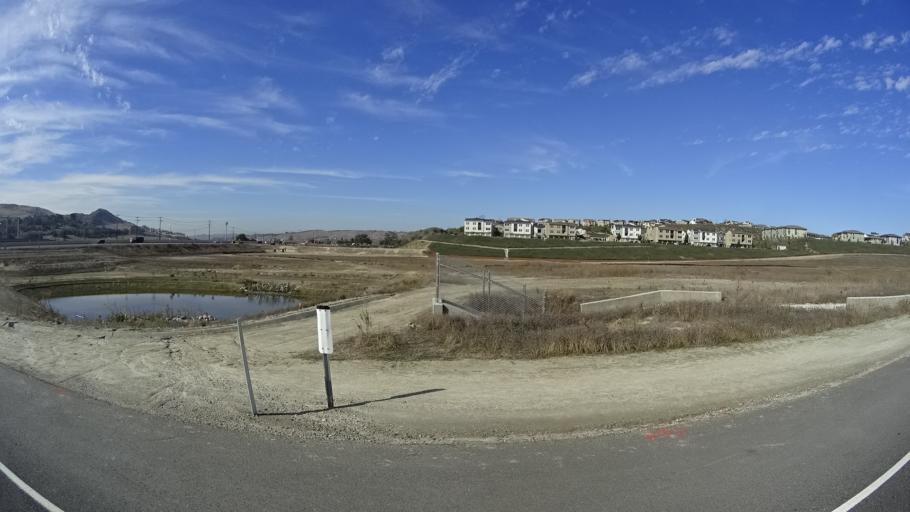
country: US
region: California
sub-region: Orange County
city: Ladera Ranch
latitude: 33.5283
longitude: -117.5970
